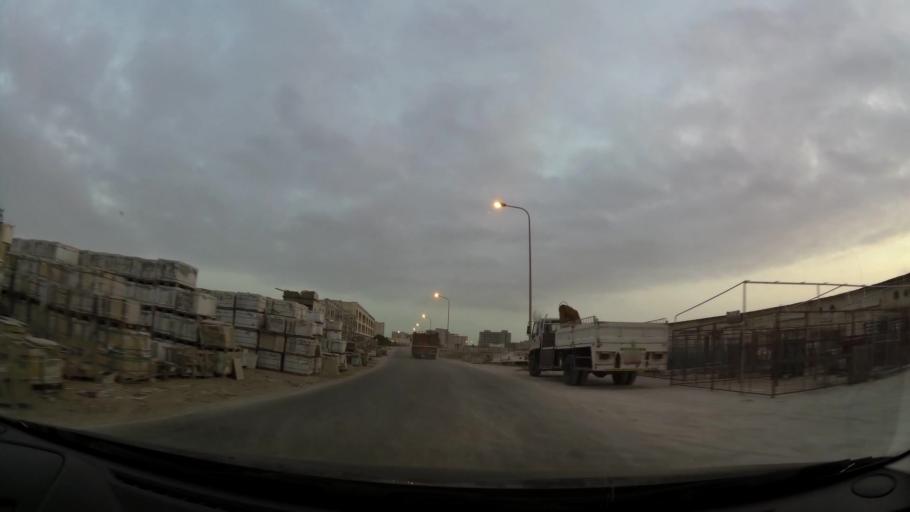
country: OM
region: Zufar
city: Salalah
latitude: 17.0309
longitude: 54.0339
